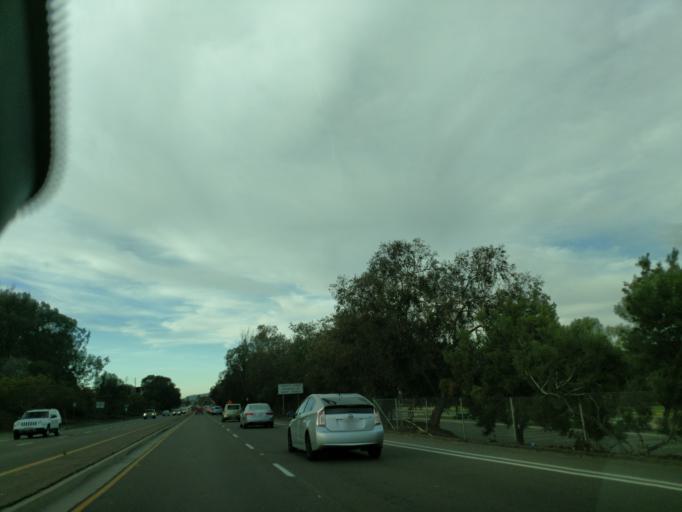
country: US
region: California
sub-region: San Diego County
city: Coronado
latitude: 32.7469
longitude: -117.2340
